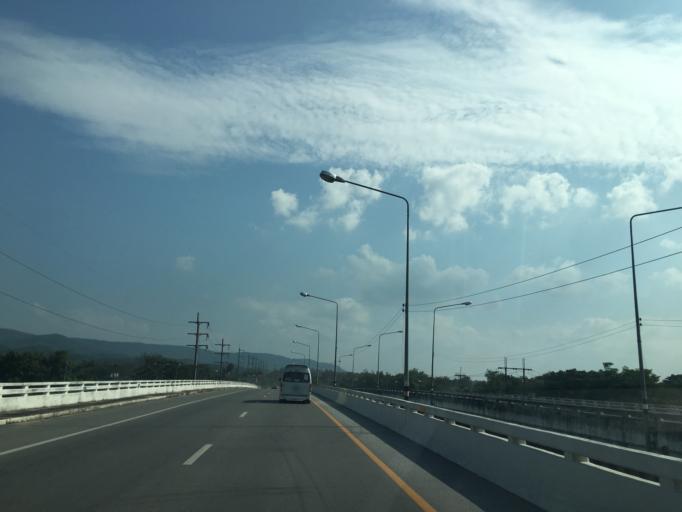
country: TH
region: Chiang Rai
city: Mae Lao
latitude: 19.7156
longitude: 99.7175
